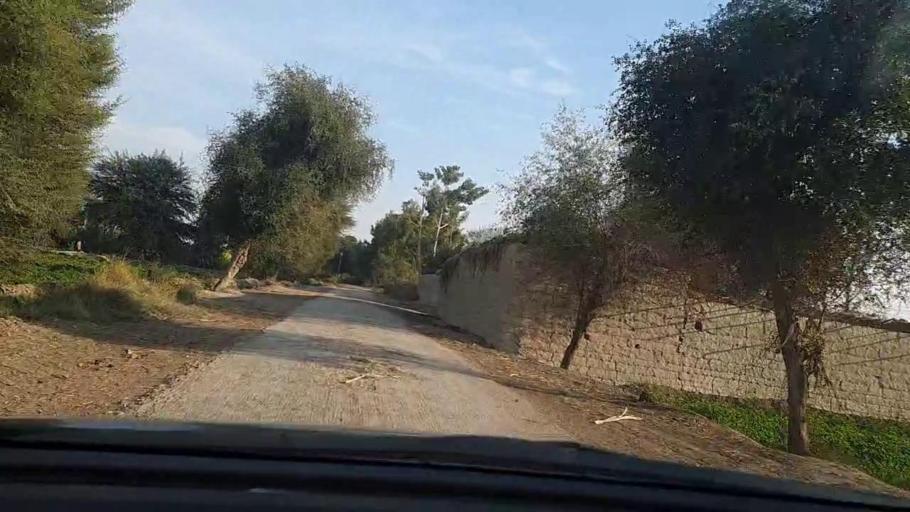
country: PK
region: Sindh
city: Daulatpur
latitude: 26.3361
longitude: 68.0375
